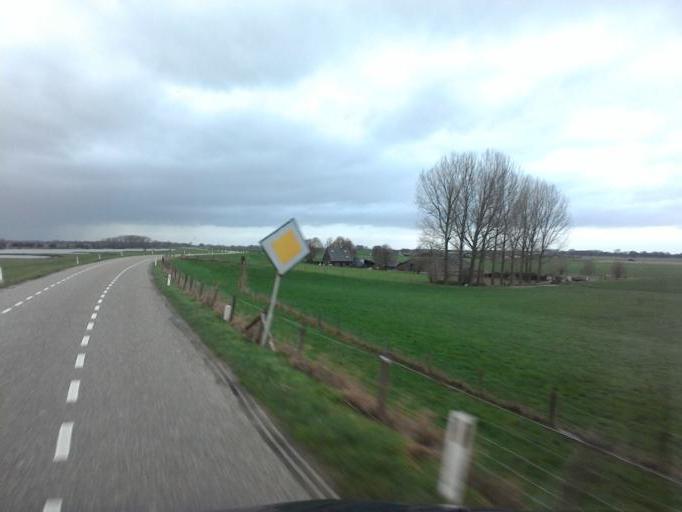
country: NL
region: Gelderland
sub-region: Gemeente Culemborg
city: Culemborg
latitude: 51.9651
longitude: 5.2812
